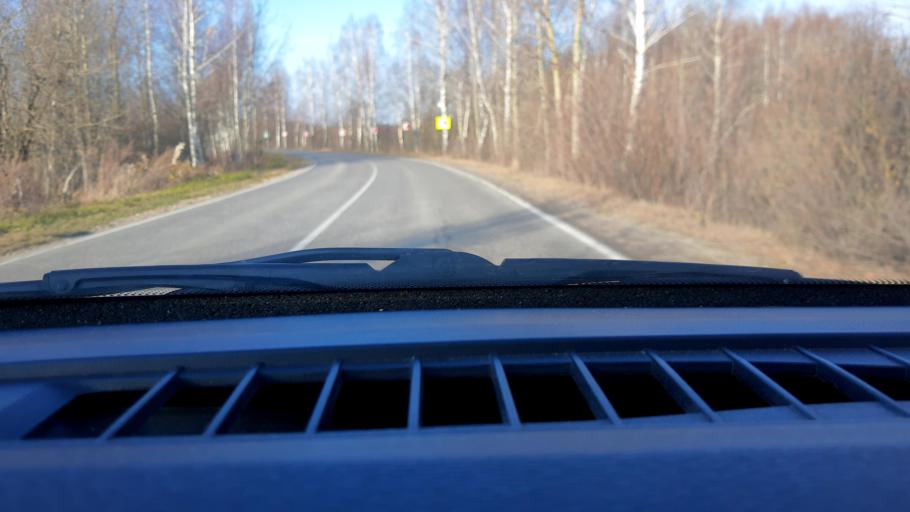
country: RU
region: Nizjnij Novgorod
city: Neklyudovo
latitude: 56.4745
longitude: 43.8823
